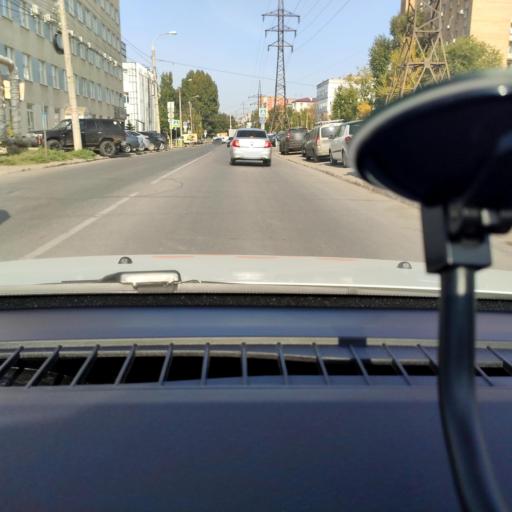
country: RU
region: Samara
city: Samara
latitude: 53.1896
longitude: 50.1721
